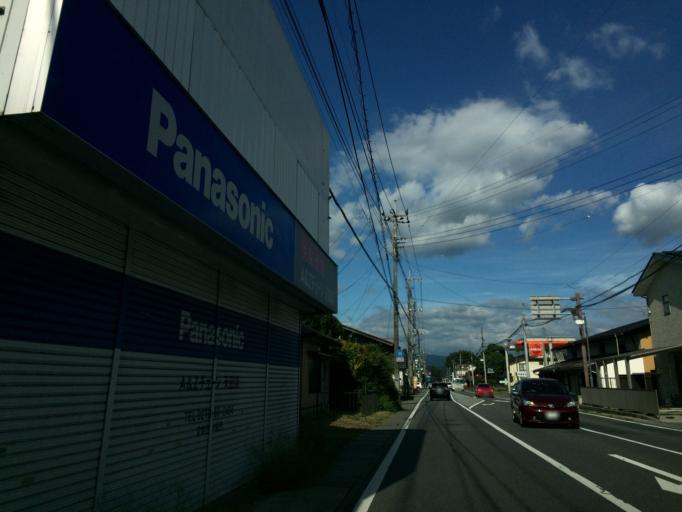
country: JP
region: Gunma
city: Nakanojomachi
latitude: 36.5721
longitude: 138.8277
